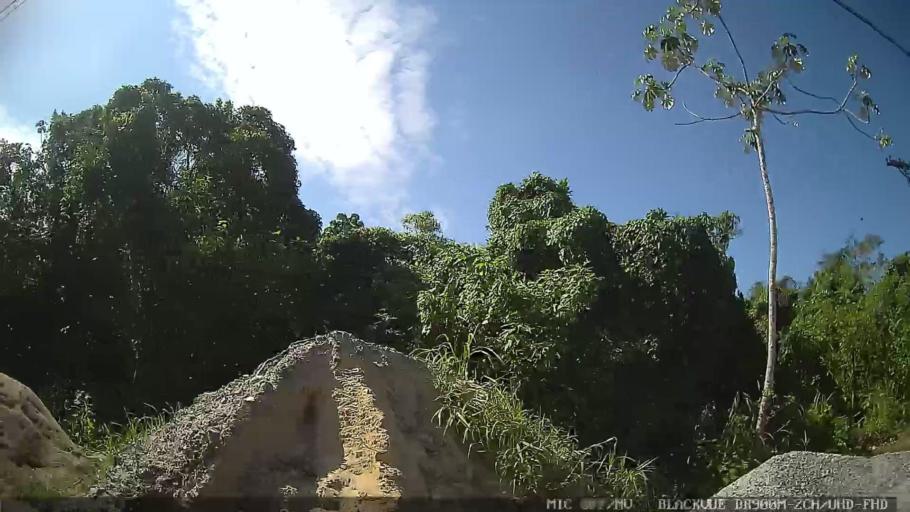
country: BR
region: Sao Paulo
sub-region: Itanhaem
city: Itanhaem
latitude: -24.1491
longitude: -46.7411
